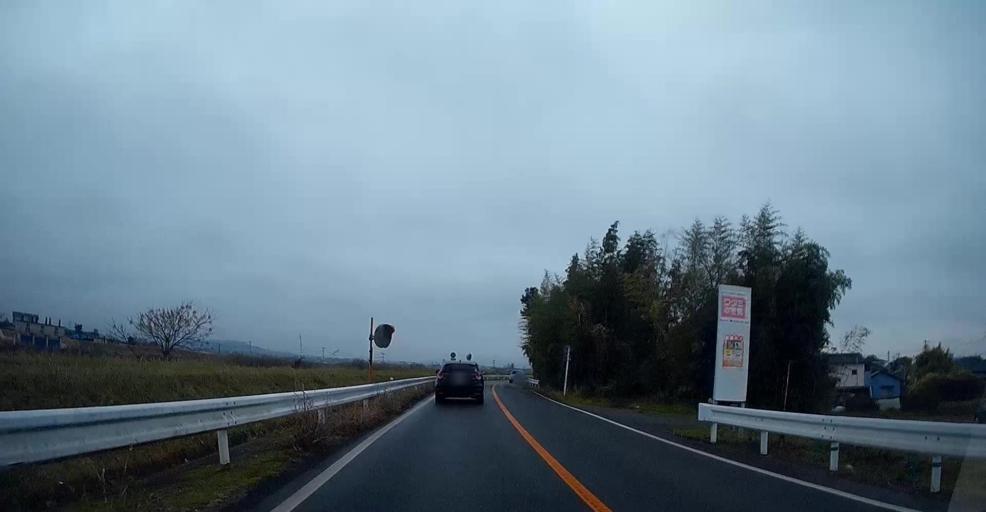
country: JP
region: Kumamoto
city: Kumamoto
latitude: 32.7560
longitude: 130.7487
